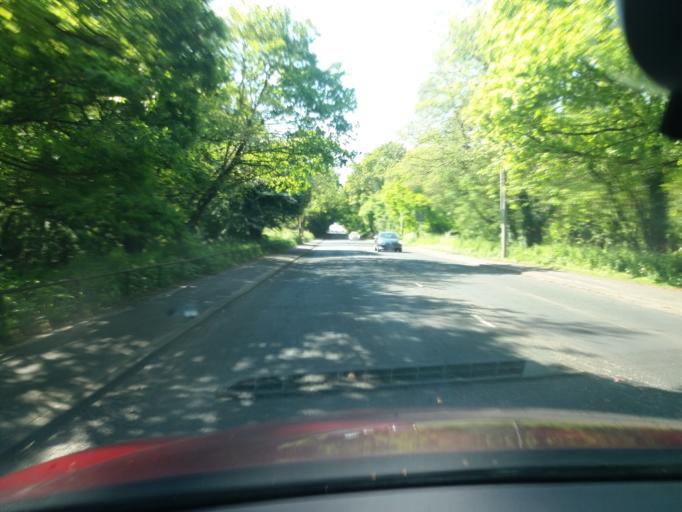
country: GB
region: England
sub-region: Lancashire
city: Coppull
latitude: 53.6319
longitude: -2.6554
